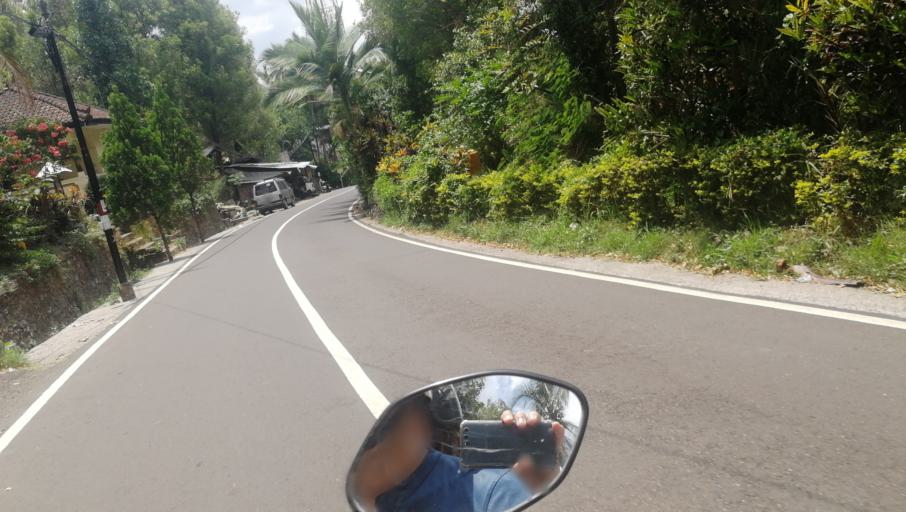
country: ID
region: Bali
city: Banjar Pedawa
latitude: -8.2634
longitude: 115.0381
